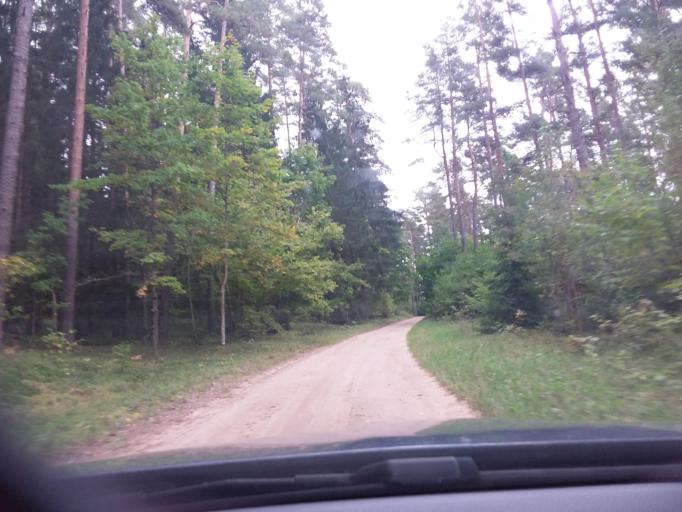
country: LV
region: Talsu Rajons
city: Stende
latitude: 57.0750
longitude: 22.3057
